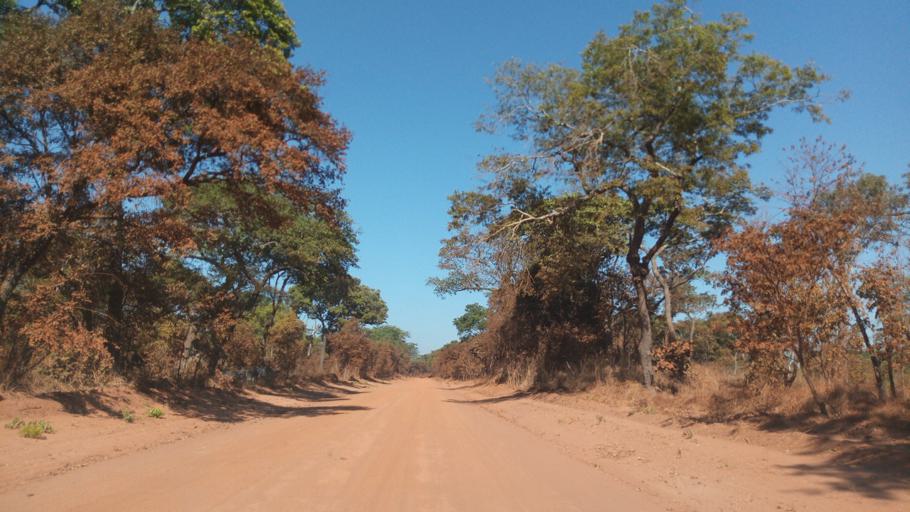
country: ZM
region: Luapula
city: Mwense
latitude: -10.7419
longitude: 28.3296
